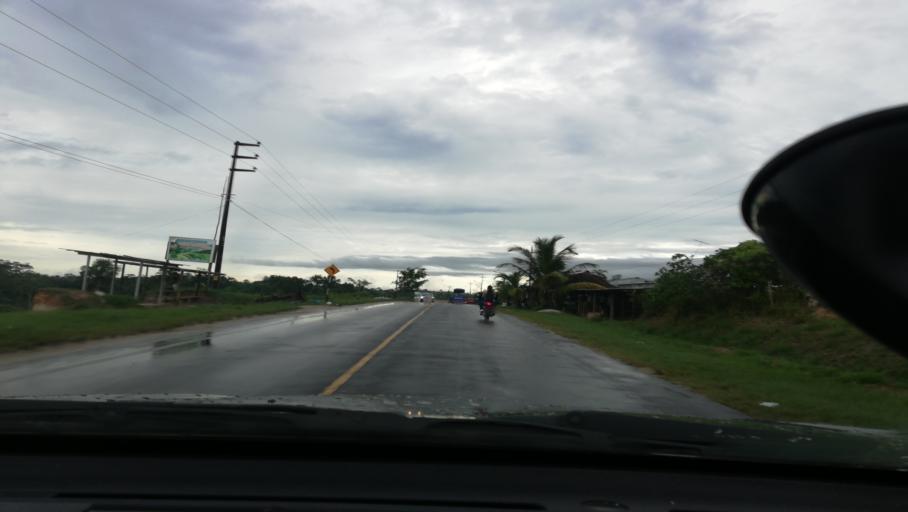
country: PE
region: Loreto
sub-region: Provincia de Maynas
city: Iquitos
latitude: -3.8556
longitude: -73.3378
